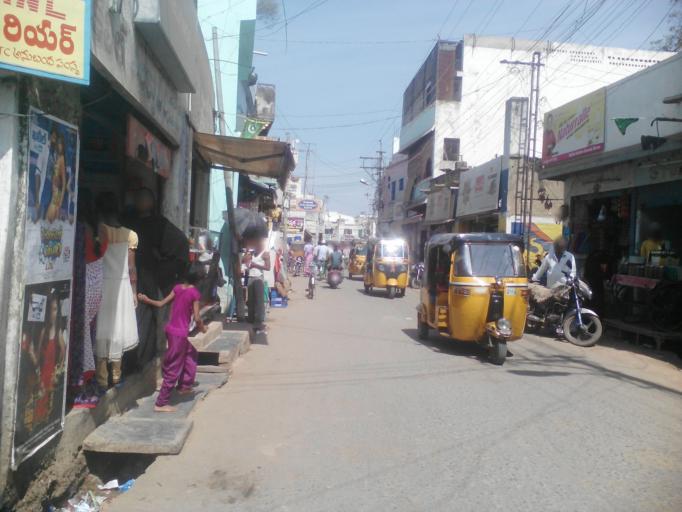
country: IN
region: Andhra Pradesh
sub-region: Kurnool
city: Nandyal
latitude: 15.4892
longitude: 78.4867
